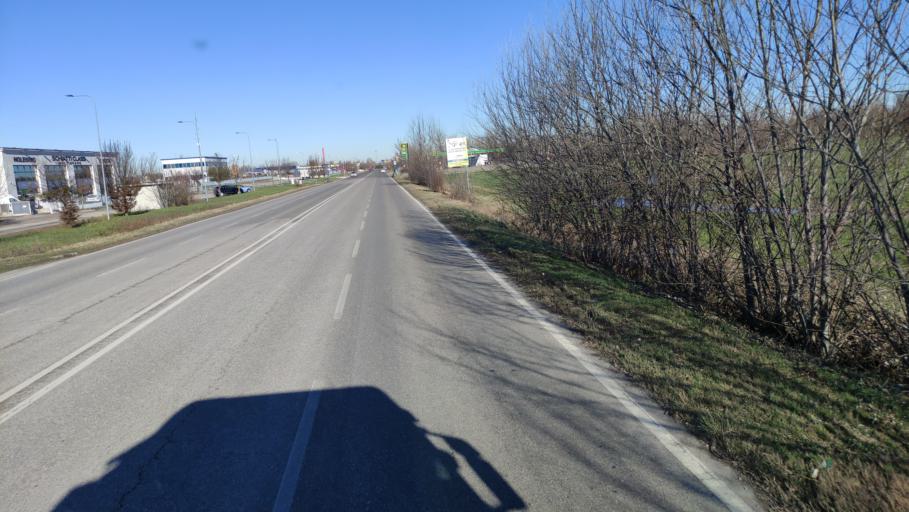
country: IT
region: Emilia-Romagna
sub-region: Provincia di Reggio Emilia
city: Correggio
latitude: 44.7529
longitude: 10.7884
